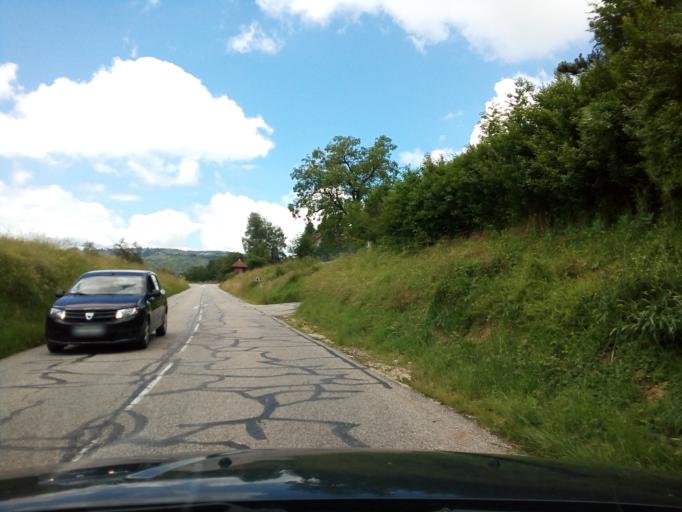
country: FR
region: Rhone-Alpes
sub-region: Departement de la Savoie
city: Les Echelles
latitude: 45.4473
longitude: 5.7531
